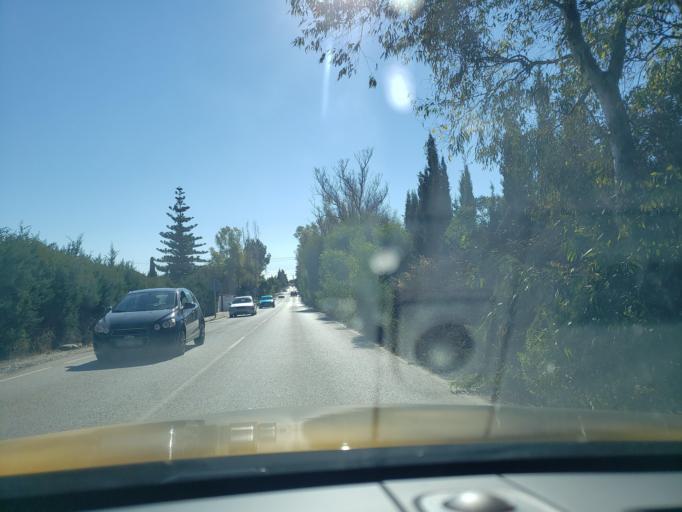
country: ES
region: Andalusia
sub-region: Provincia de Malaga
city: Benahavis
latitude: 36.4844
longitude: -5.0154
